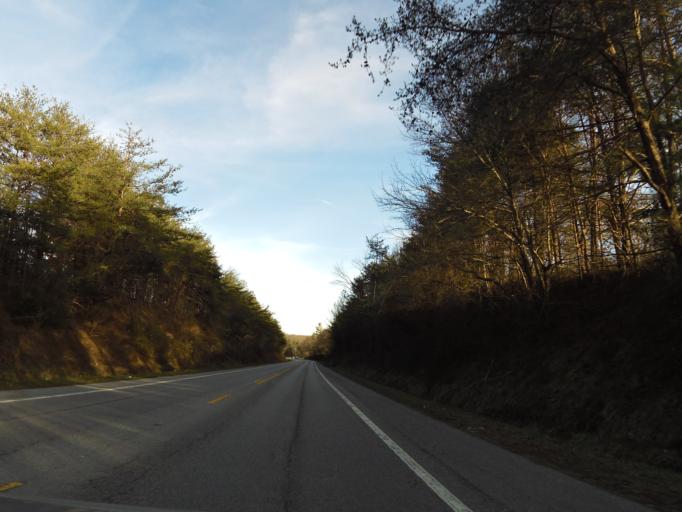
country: US
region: Tennessee
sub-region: Cumberland County
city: Crossville
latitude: 35.9525
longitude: -85.1062
